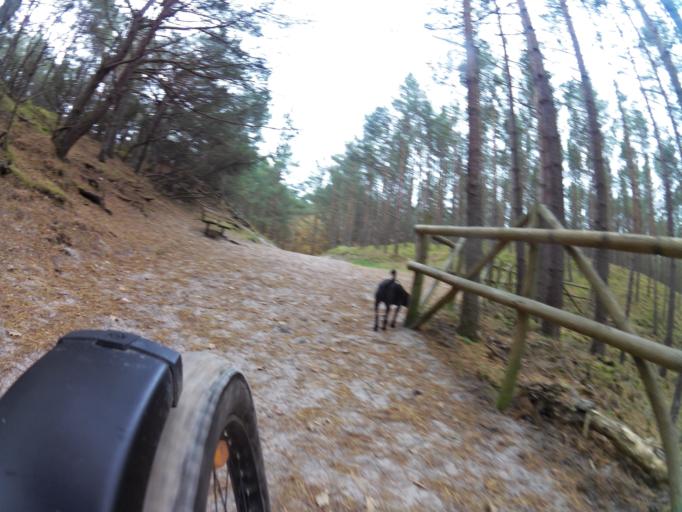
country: PL
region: Pomeranian Voivodeship
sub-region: Powiat pucki
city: Krokowa
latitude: 54.8315
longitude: 18.1423
